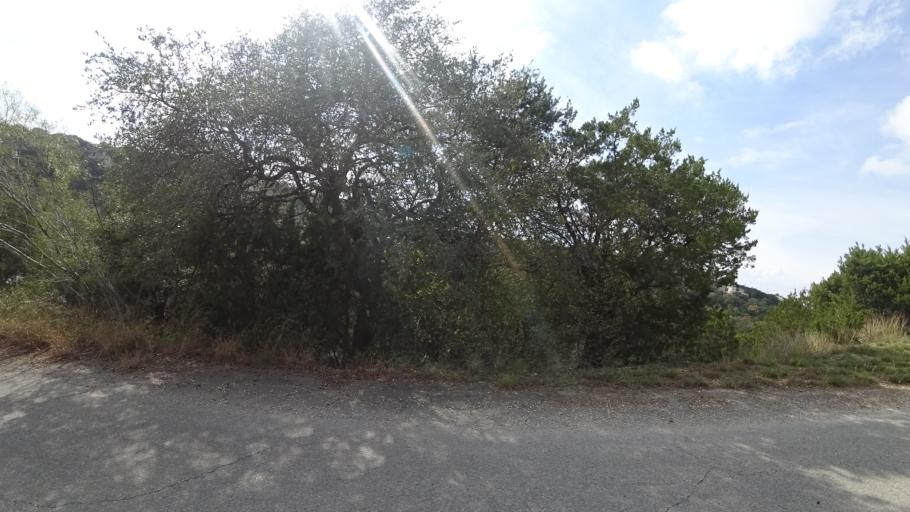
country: US
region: Texas
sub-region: Travis County
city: Hudson Bend
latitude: 30.3786
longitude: -97.9178
